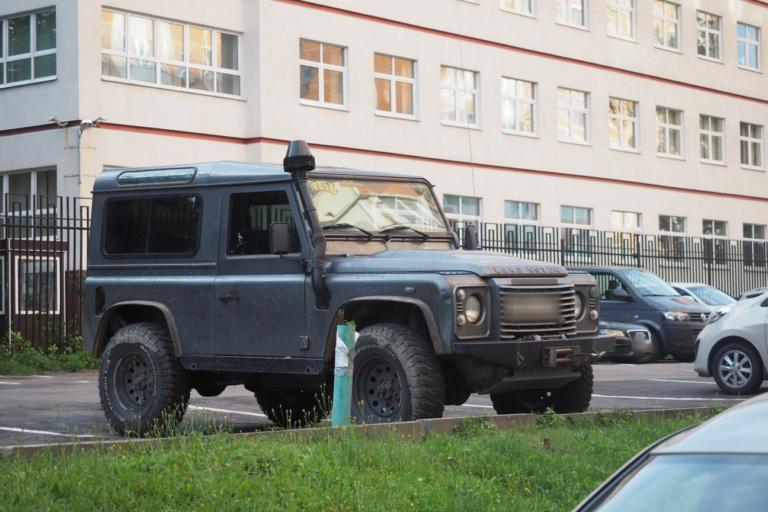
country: RU
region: Moskovskaya
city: Cheremushki
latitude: 55.6712
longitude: 37.5750
